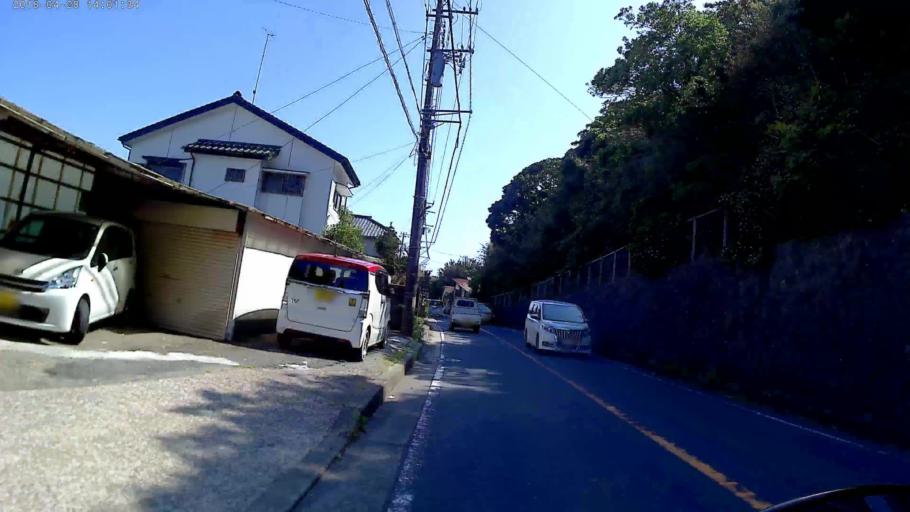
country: JP
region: Kanagawa
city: Miura
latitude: 35.1674
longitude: 139.6593
